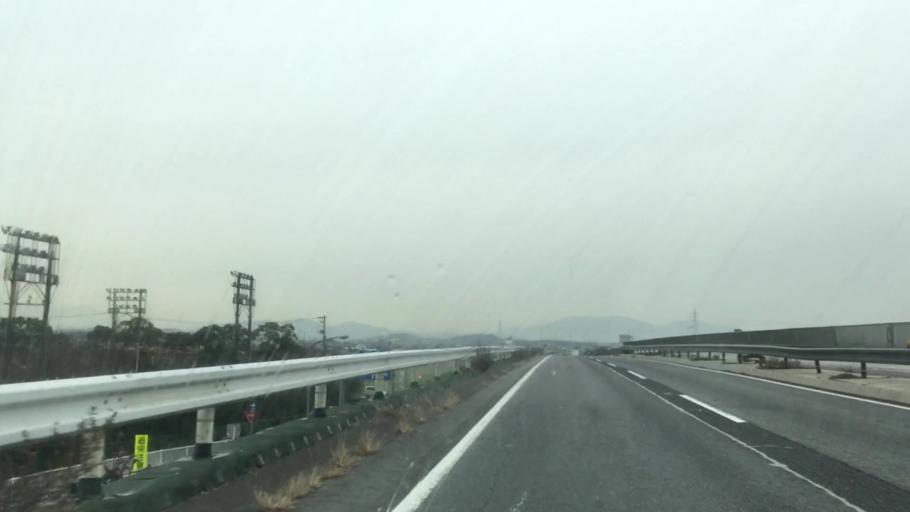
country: JP
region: Aichi
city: Nishio
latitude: 34.8998
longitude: 137.0703
